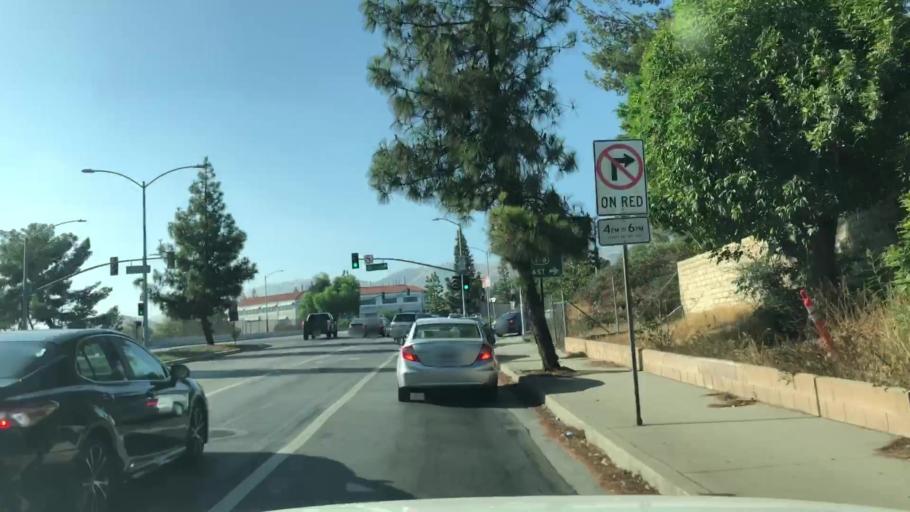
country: US
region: California
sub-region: Los Angeles County
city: Northridge
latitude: 34.2714
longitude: -118.5556
